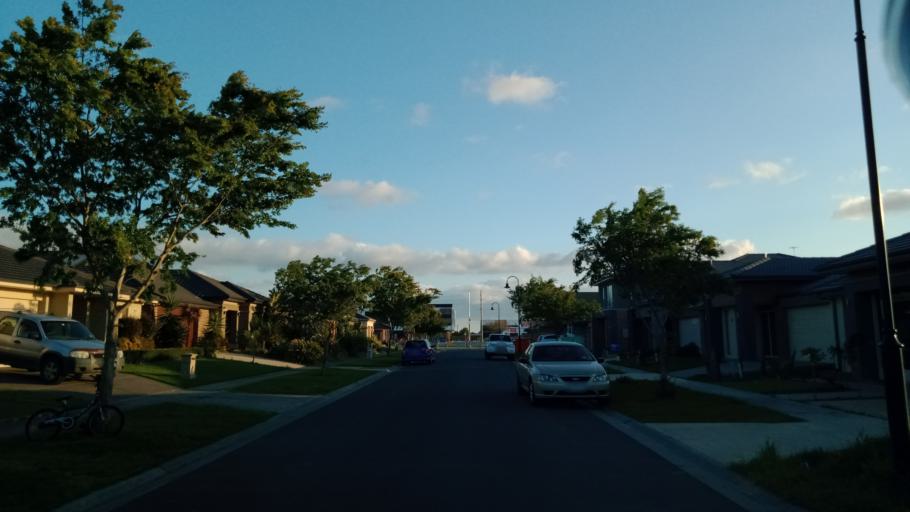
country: AU
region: Victoria
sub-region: Casey
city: Cranbourne West
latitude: -38.0783
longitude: 145.2573
